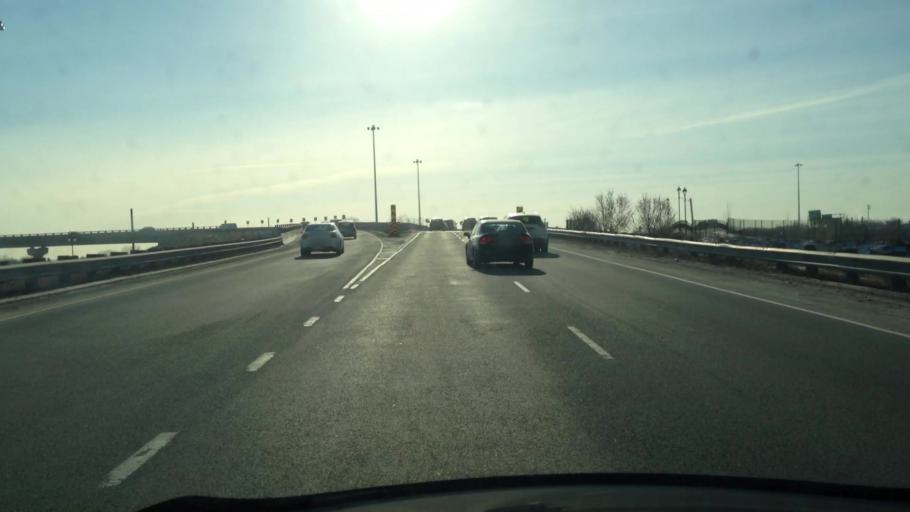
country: CA
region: Quebec
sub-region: Laurentides
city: Boisbriand
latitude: 45.6284
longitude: -73.8438
